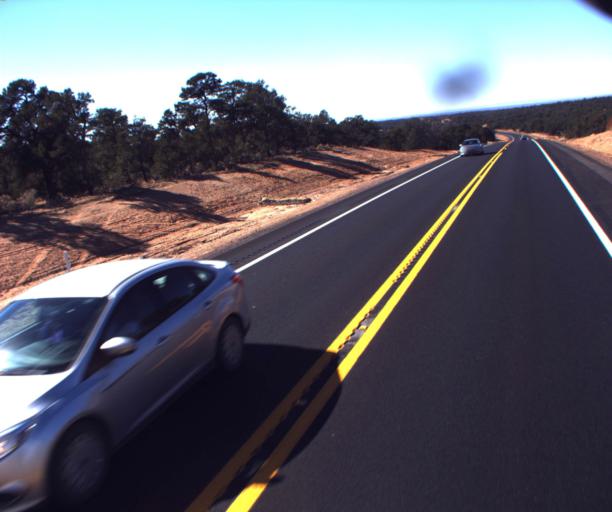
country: US
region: Arizona
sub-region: Apache County
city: Ganado
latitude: 35.7139
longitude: -109.3355
